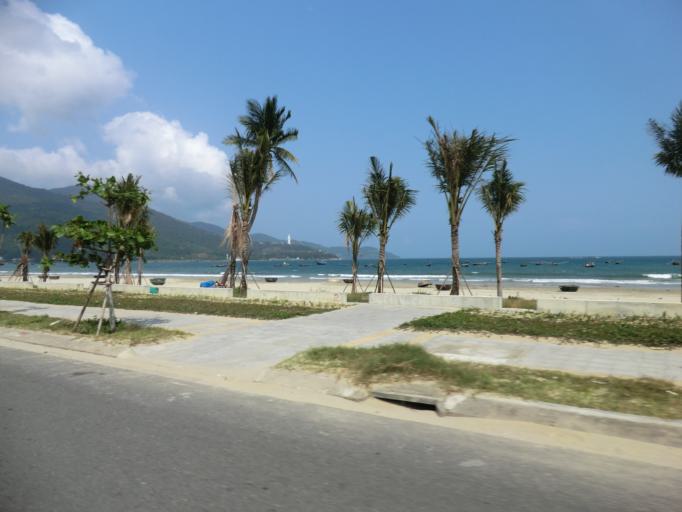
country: VN
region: Da Nang
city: Son Tra
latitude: 16.0916
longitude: 108.2509
